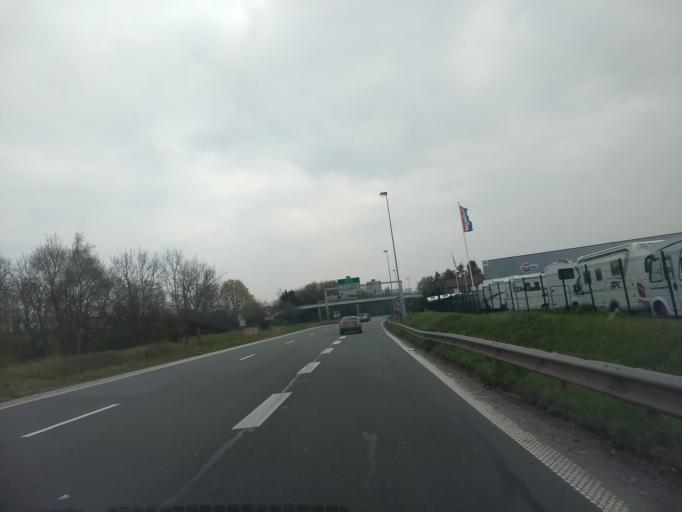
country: FR
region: Nord-Pas-de-Calais
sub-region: Departement du Pas-de-Calais
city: Saint-Nicolas
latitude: 50.3055
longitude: 2.7842
